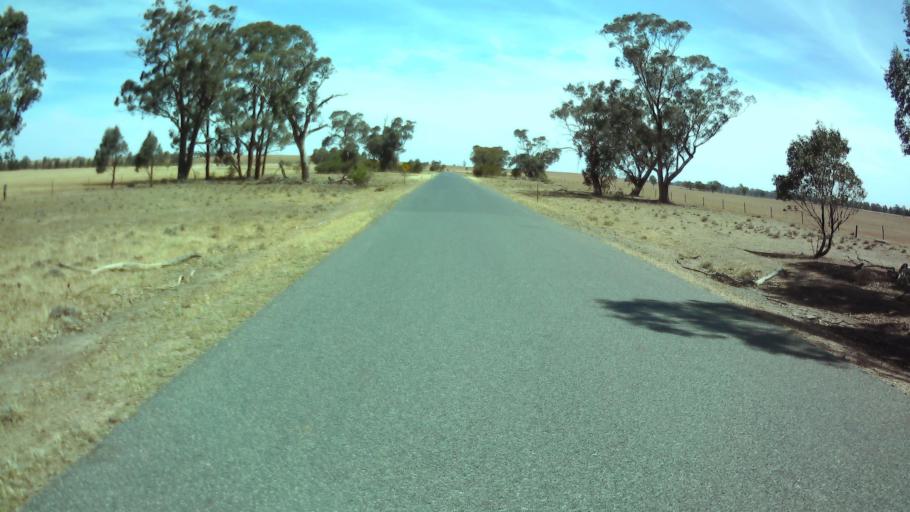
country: AU
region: New South Wales
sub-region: Weddin
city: Grenfell
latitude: -33.8842
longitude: 147.7423
